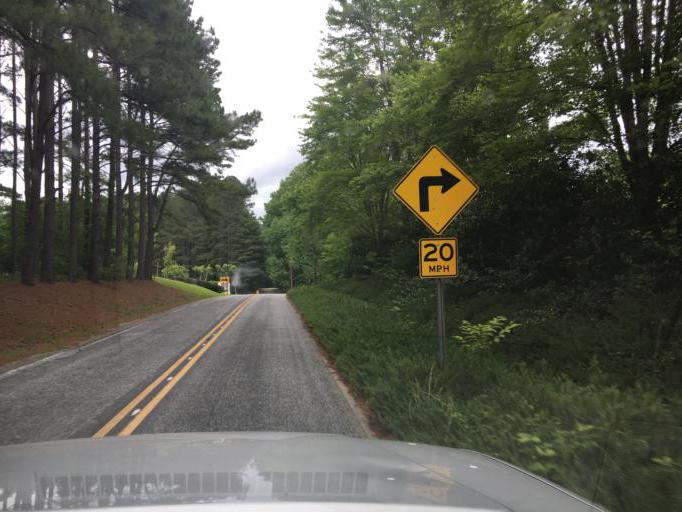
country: US
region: South Carolina
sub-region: Greenville County
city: Tigerville
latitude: 35.1364
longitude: -82.4138
